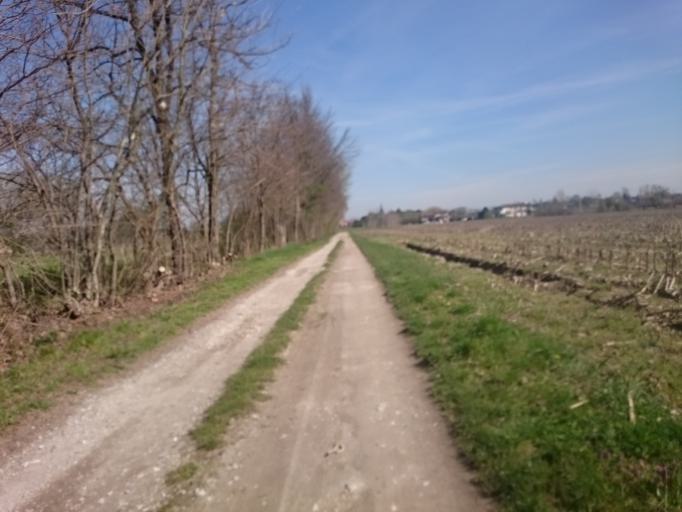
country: IT
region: Veneto
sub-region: Provincia di Padova
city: Sarmeola
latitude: 45.4308
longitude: 11.8303
